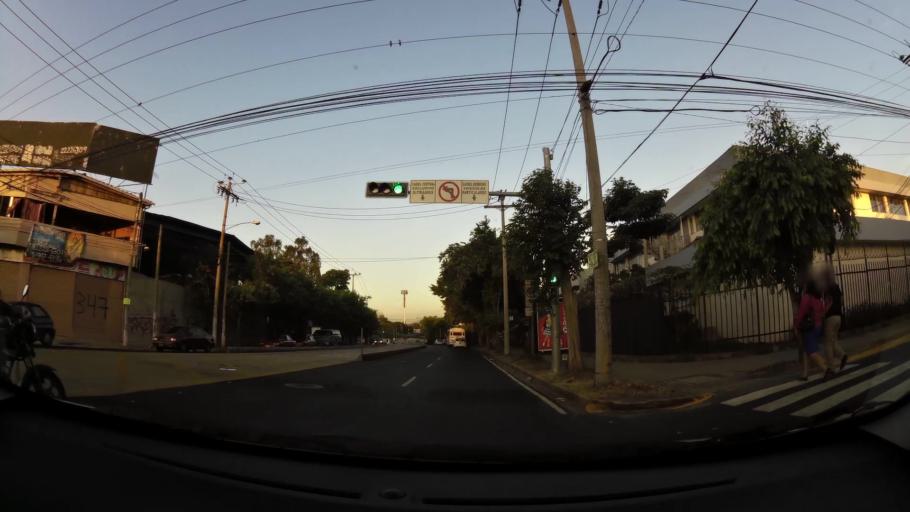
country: SV
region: San Salvador
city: San Salvador
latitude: 13.7035
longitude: -89.1996
